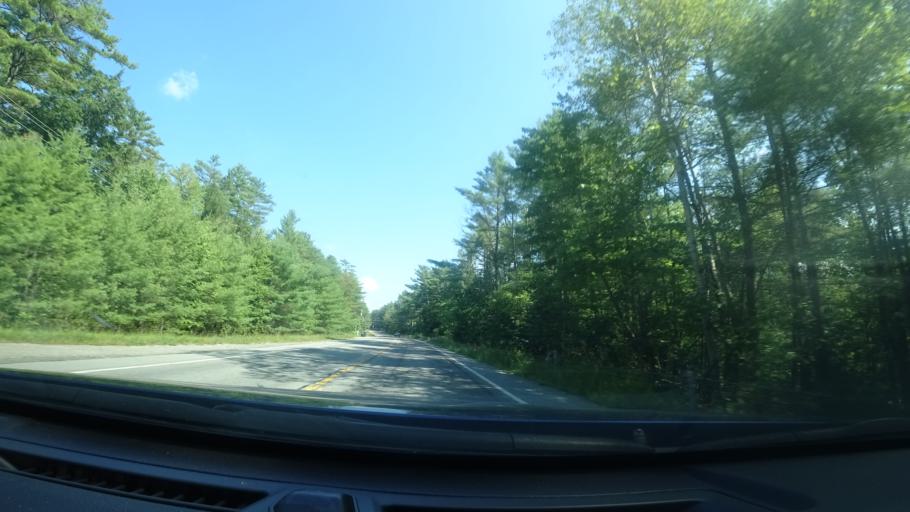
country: US
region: New York
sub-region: Warren County
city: Warrensburg
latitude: 43.6369
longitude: -73.7978
